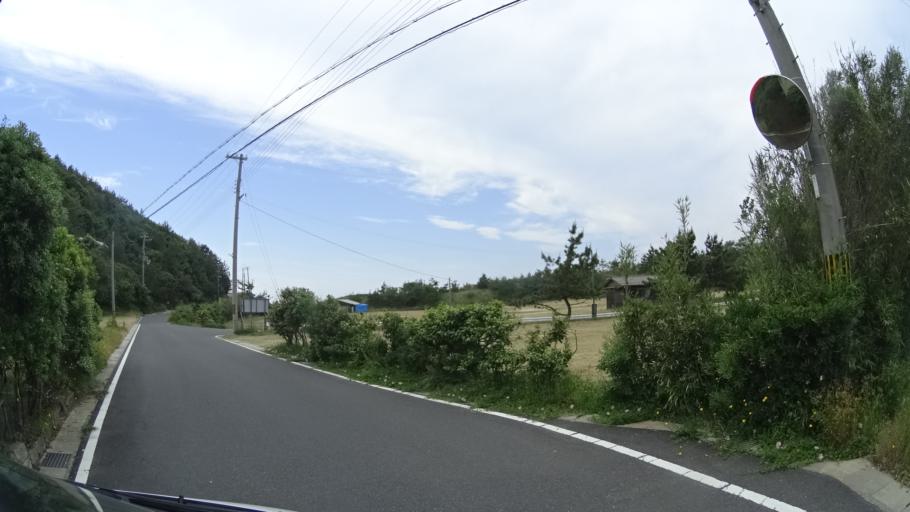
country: JP
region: Kyoto
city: Miyazu
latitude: 35.7010
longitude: 135.0526
